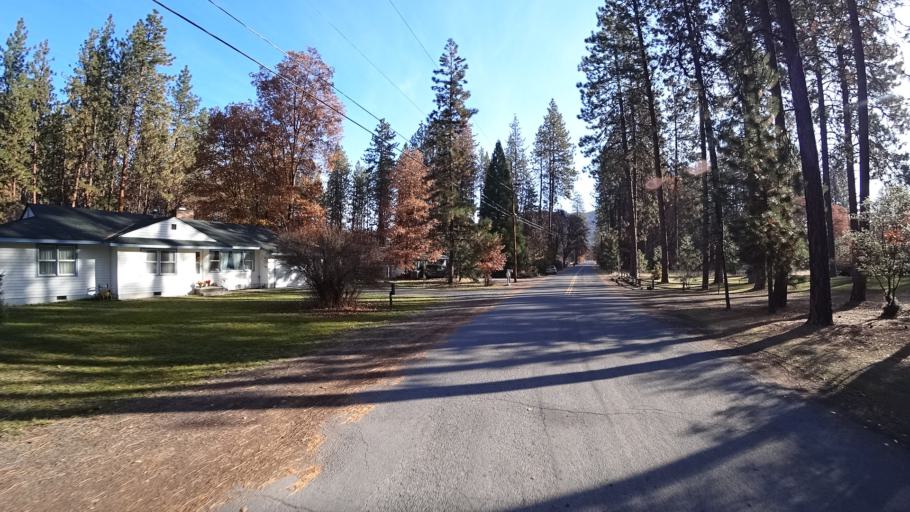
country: US
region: California
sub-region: Siskiyou County
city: Yreka
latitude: 41.6878
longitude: -122.6409
